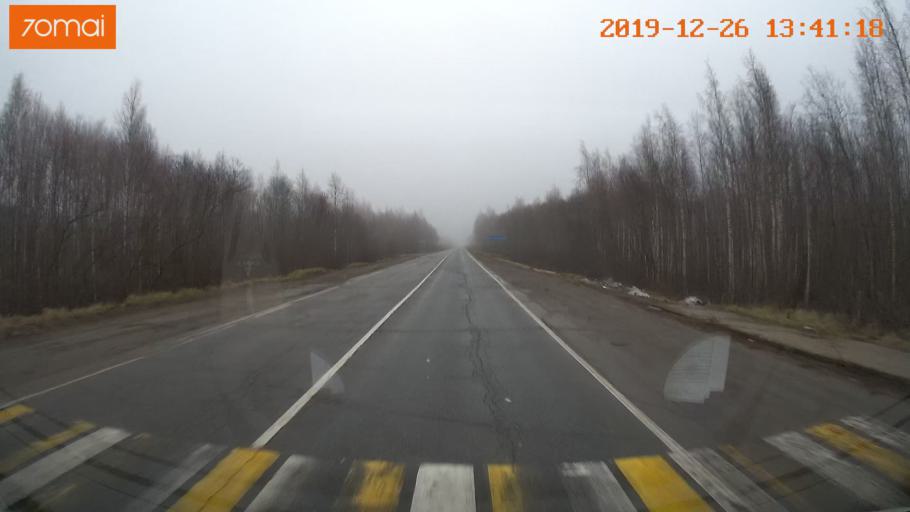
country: RU
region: Vologda
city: Sheksna
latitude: 58.7329
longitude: 38.4467
